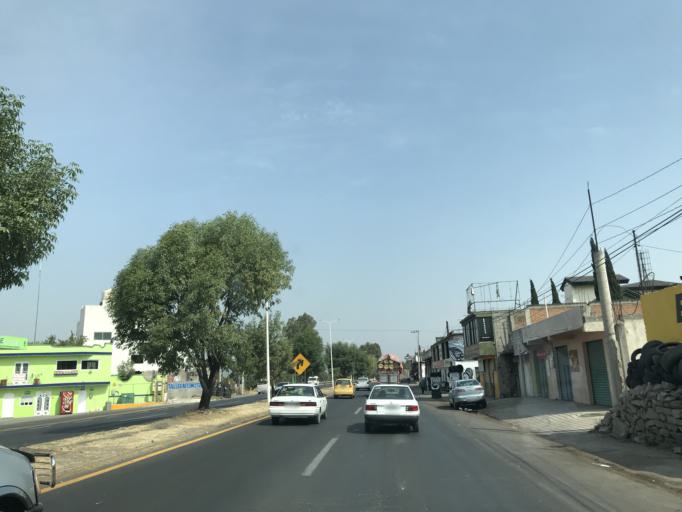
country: MX
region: Tlaxcala
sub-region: Teolocholco
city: Teolocholco
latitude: 19.2538
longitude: -98.1984
